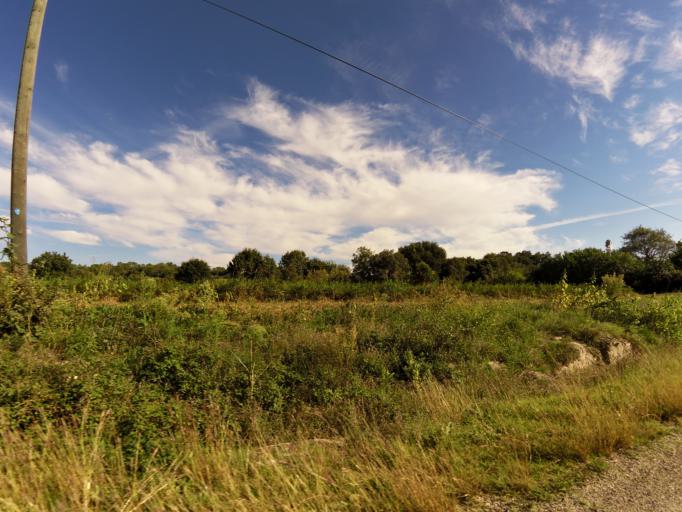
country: FR
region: Languedoc-Roussillon
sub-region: Departement du Gard
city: Villevieille
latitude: 43.7949
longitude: 4.1185
